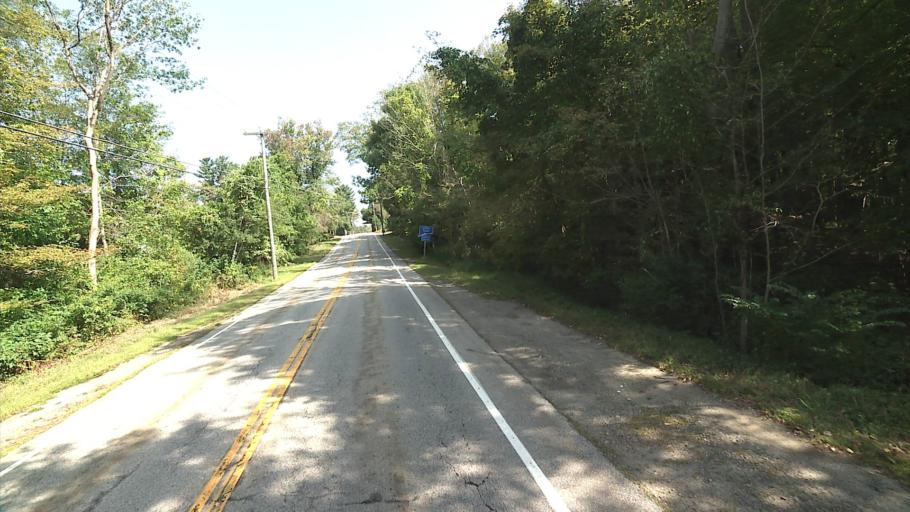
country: US
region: Connecticut
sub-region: Windham County
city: South Woodstock
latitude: 41.8992
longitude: -71.9614
